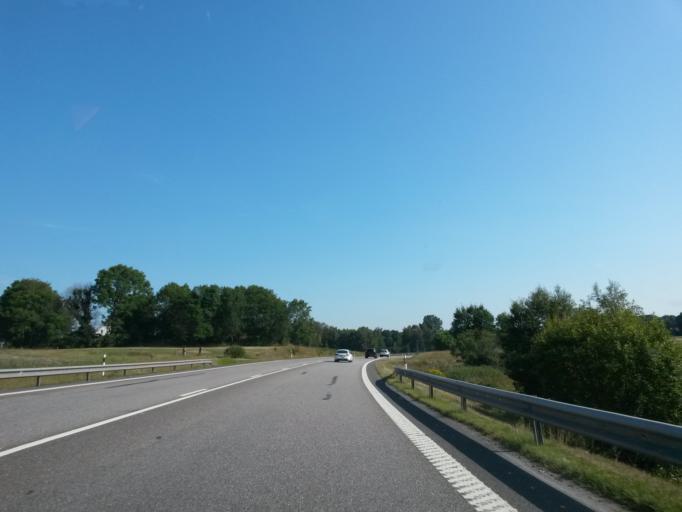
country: SE
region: Vaestra Goetaland
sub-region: Vargarda Kommun
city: Vargarda
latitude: 58.0971
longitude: 12.8305
